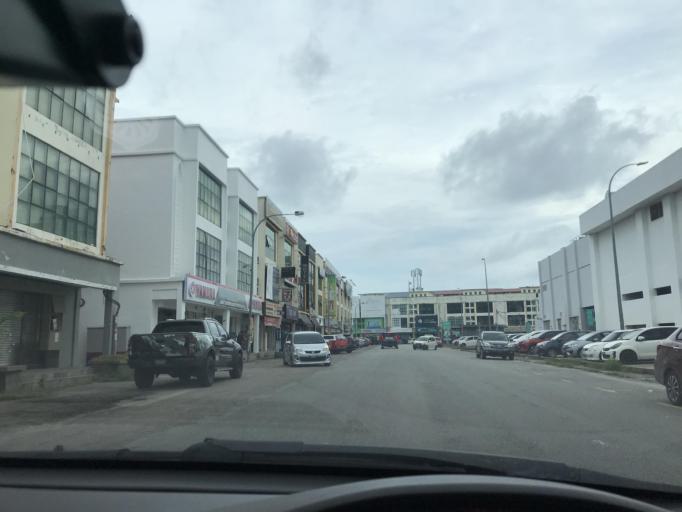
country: MY
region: Kelantan
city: Kota Bharu
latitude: 6.1143
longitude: 102.2326
